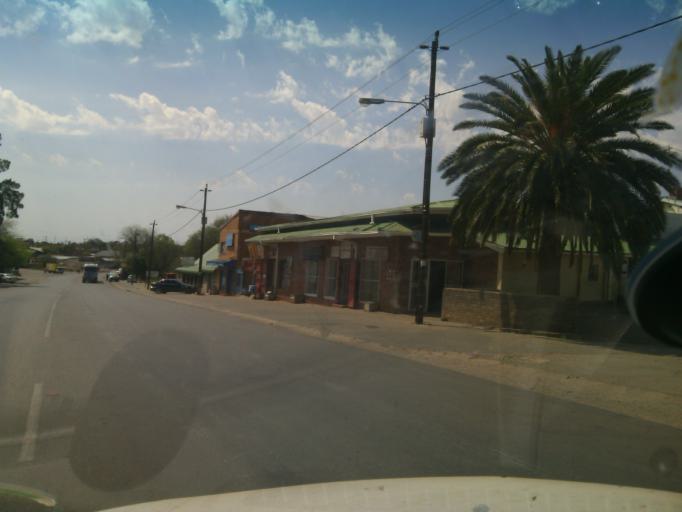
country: ZA
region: Northern Cape
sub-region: Frances Baard District Municipality
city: Barkly West
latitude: -28.5379
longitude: 24.5214
